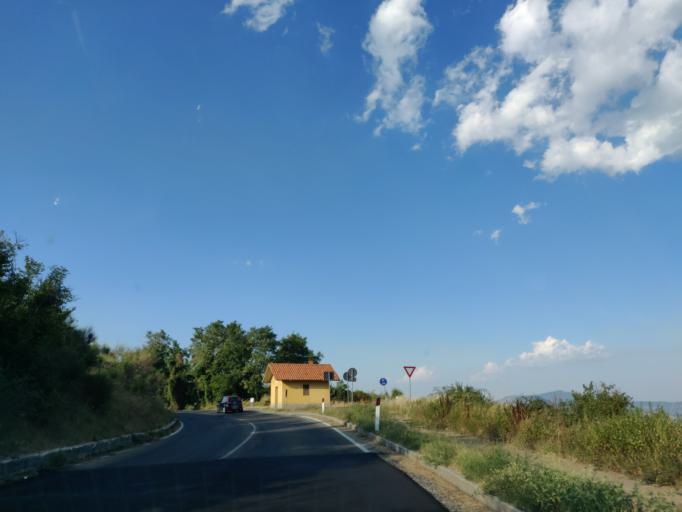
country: IT
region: Tuscany
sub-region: Provincia di Siena
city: Abbadia San Salvatore
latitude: 42.8670
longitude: 11.6811
